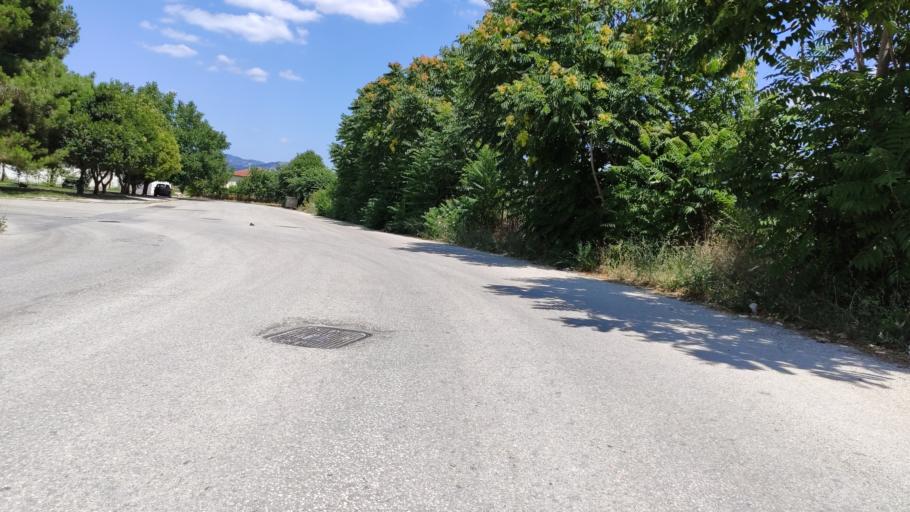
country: GR
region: East Macedonia and Thrace
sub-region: Nomos Rodopis
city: Komotini
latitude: 41.1246
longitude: 25.4002
